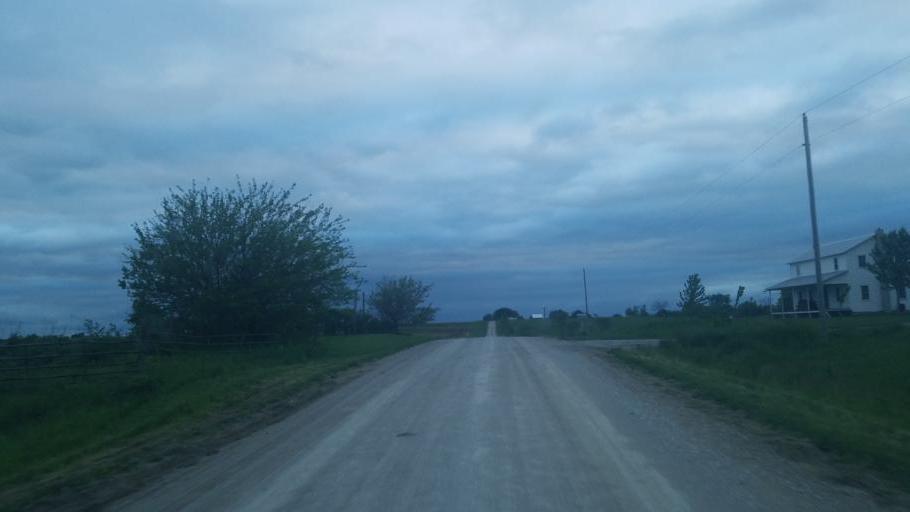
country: US
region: Iowa
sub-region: Decatur County
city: Lamoni
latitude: 40.5947
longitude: -93.9560
